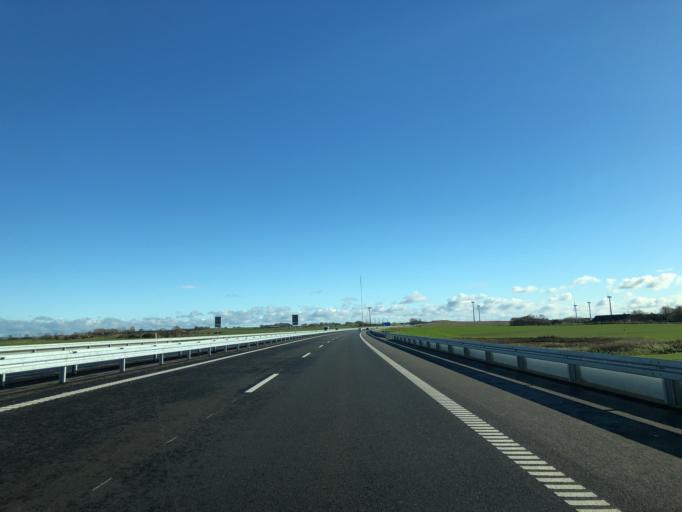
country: DK
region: Central Jutland
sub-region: Holstebro Kommune
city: Holstebro
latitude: 56.3887
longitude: 8.6344
